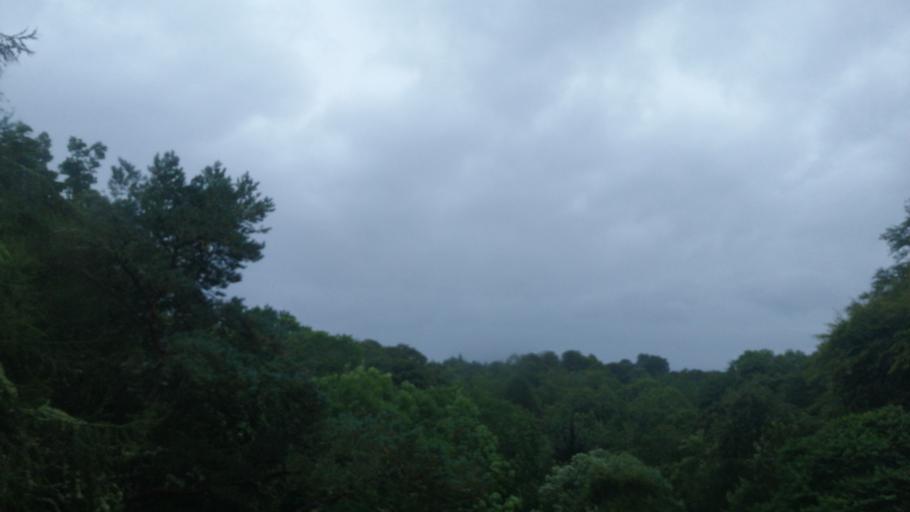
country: GB
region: Scotland
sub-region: Highland
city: Golspie
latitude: 57.9809
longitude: -3.9625
